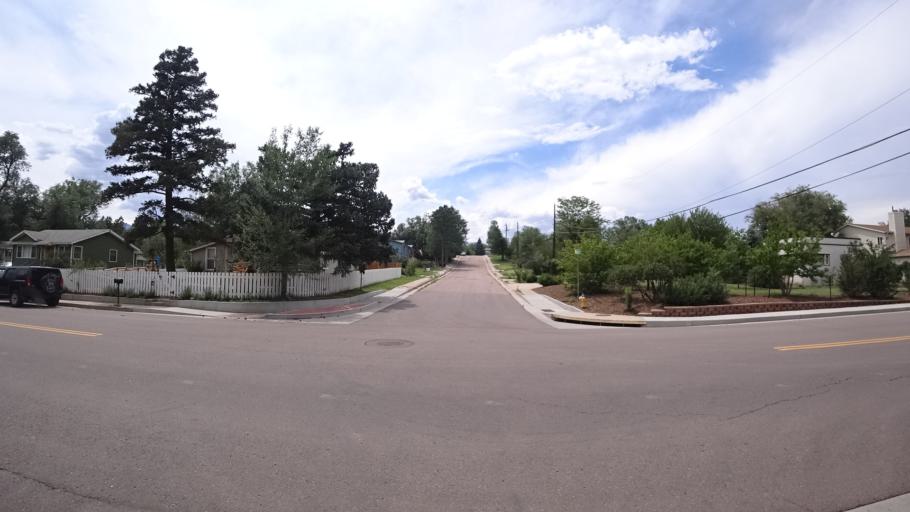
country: US
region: Colorado
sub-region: El Paso County
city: Colorado Springs
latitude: 38.8582
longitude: -104.8357
